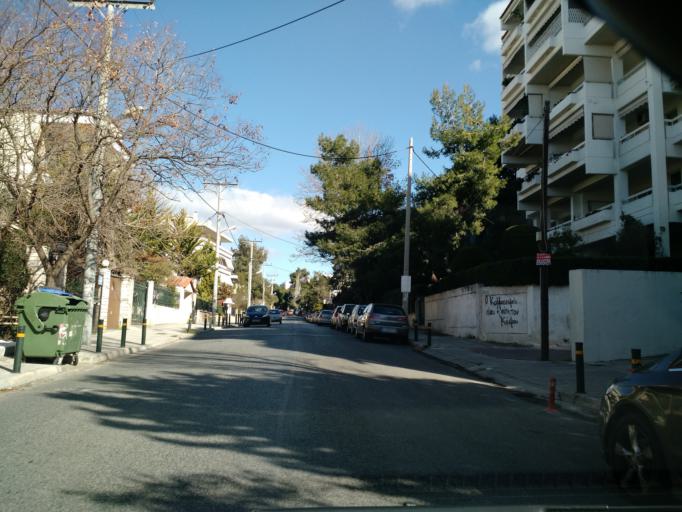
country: GR
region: Attica
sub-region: Nomarchia Athinas
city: Cholargos
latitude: 37.9997
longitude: 23.8175
